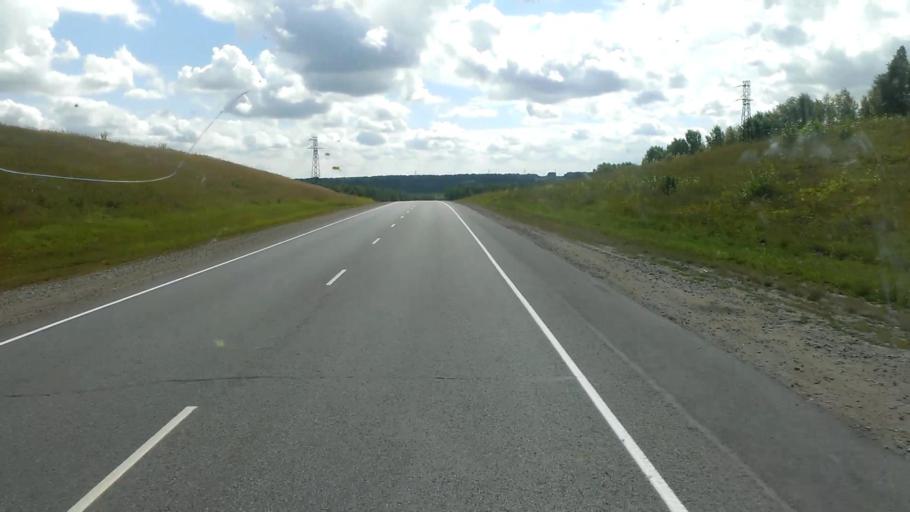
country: RU
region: Altai Krai
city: Troitskoye
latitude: 52.9450
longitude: 84.7743
